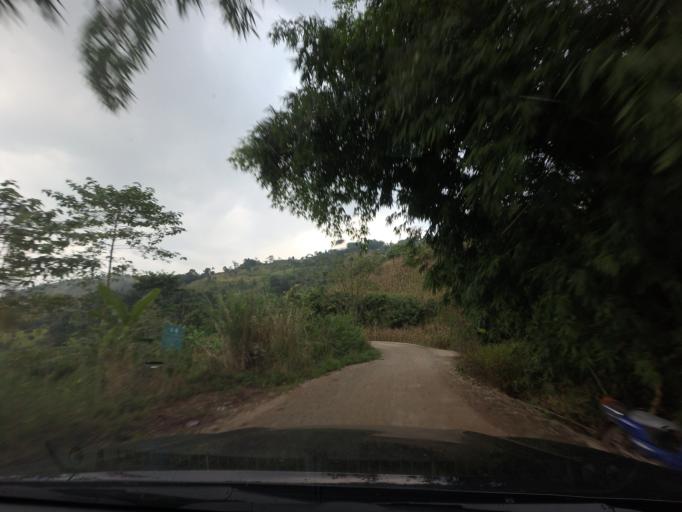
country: TH
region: Nan
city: Bo Kluea
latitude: 19.3522
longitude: 101.1718
